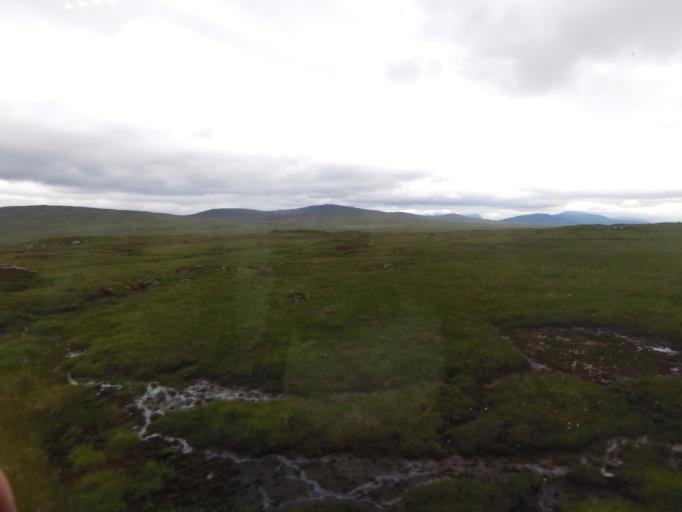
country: GB
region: Scotland
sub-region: Highland
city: Spean Bridge
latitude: 56.7211
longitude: -4.6238
